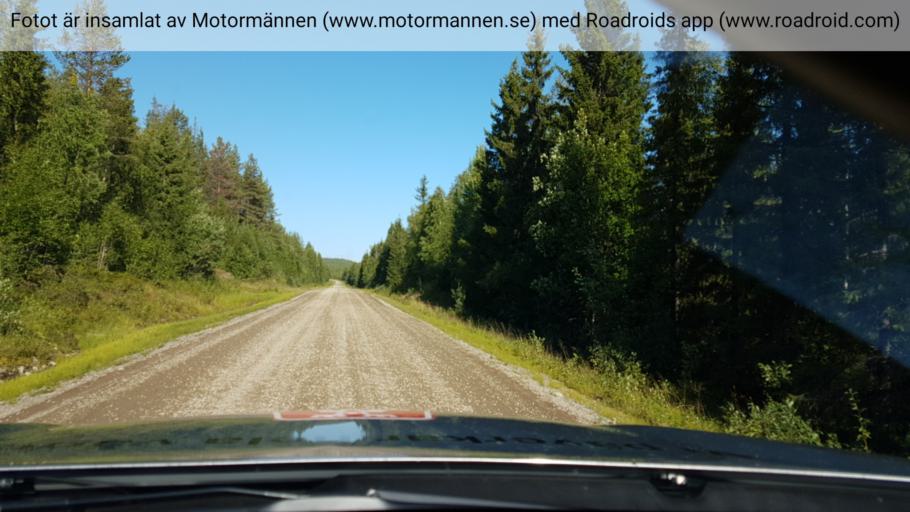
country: SE
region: Norrbotten
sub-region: Kalix Kommun
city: Kalix
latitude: 66.2083
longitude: 23.1891
